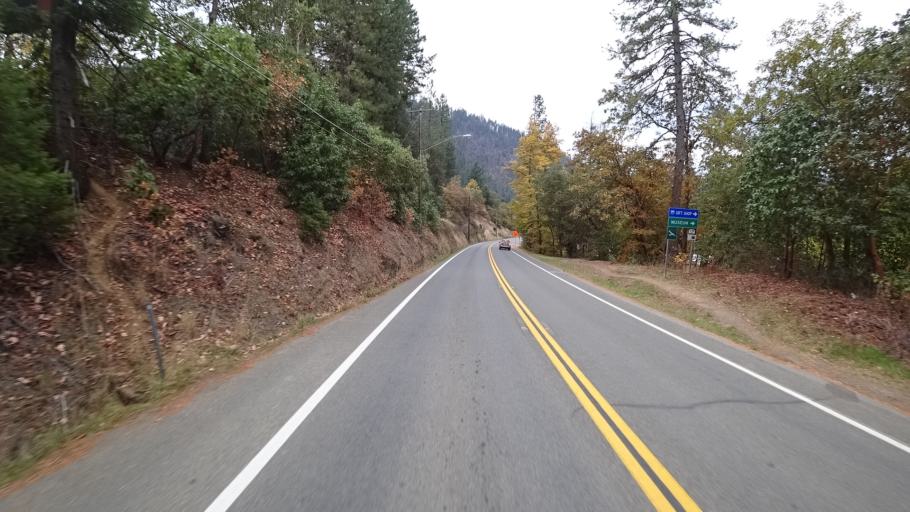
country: US
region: California
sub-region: Siskiyou County
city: Happy Camp
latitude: 41.7942
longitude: -123.3757
